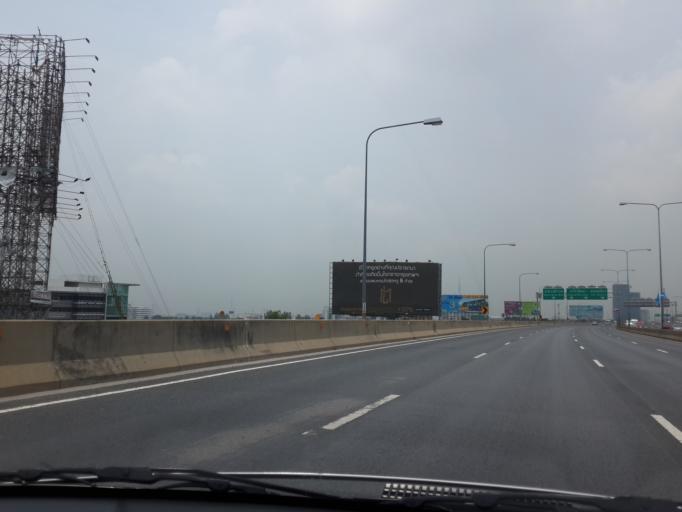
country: TH
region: Bangkok
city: Chatuchak
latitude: 13.8393
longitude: 100.5576
